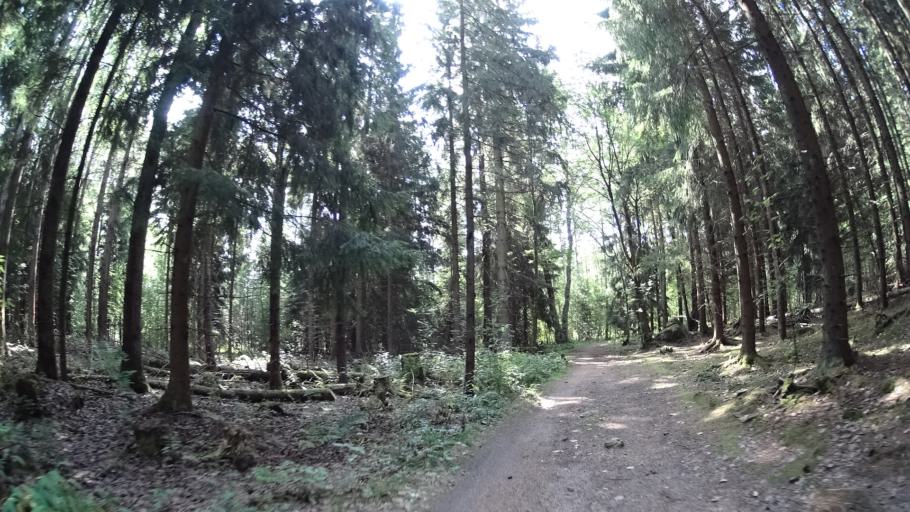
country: FI
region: Uusimaa
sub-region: Helsinki
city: Teekkarikylae
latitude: 60.2723
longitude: 24.9029
